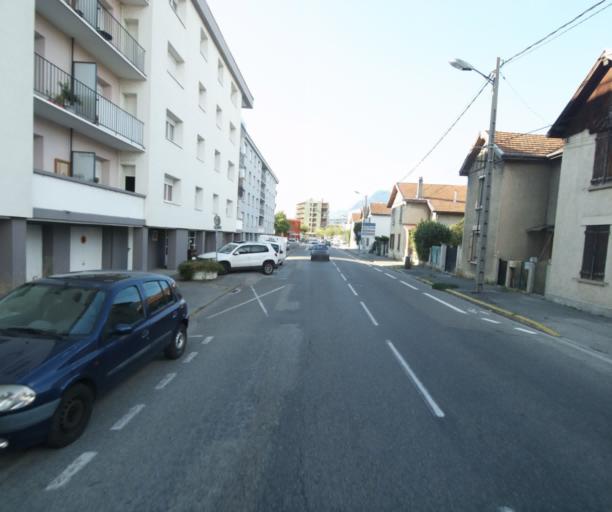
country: FR
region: Rhone-Alpes
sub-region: Departement de l'Isere
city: Fontaine
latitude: 45.1959
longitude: 5.6941
